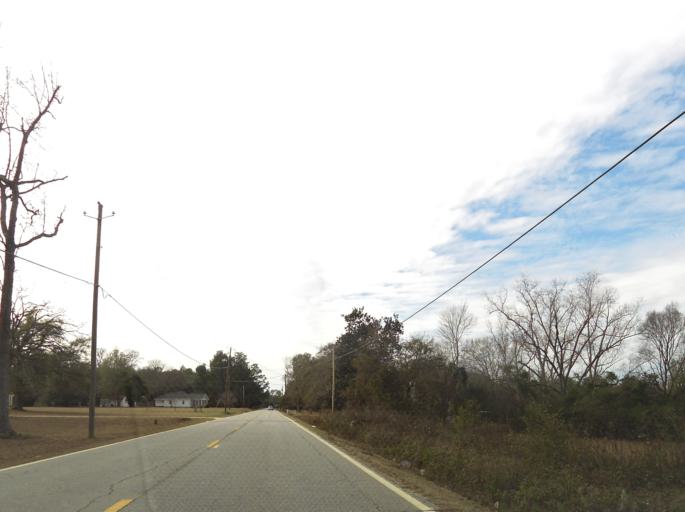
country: US
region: Georgia
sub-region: Bibb County
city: West Point
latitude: 32.8041
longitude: -83.8015
